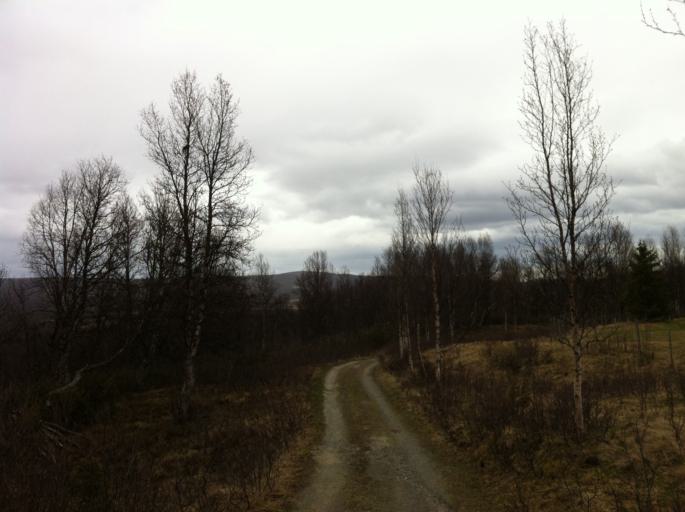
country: NO
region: Sor-Trondelag
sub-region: Tydal
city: Aas
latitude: 62.7068
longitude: 12.4890
